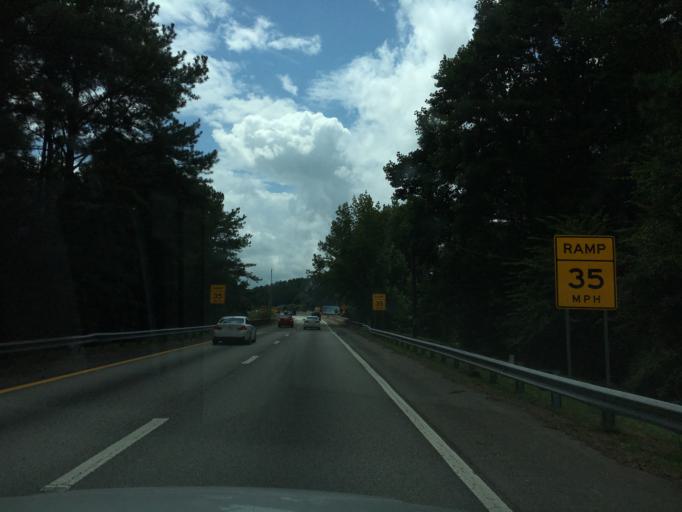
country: US
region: Georgia
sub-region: DeKalb County
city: Panthersville
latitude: 33.7174
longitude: -84.2407
